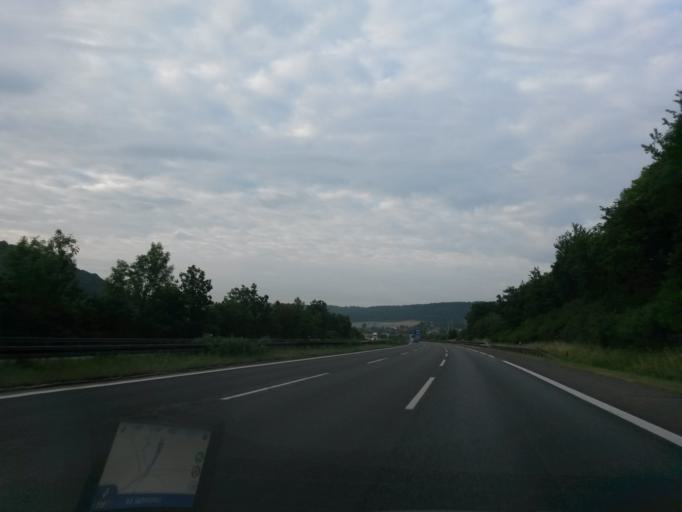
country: DE
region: Bavaria
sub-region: Regierungsbezirk Mittelfranken
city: Thalmassing
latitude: 49.0847
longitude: 11.2884
